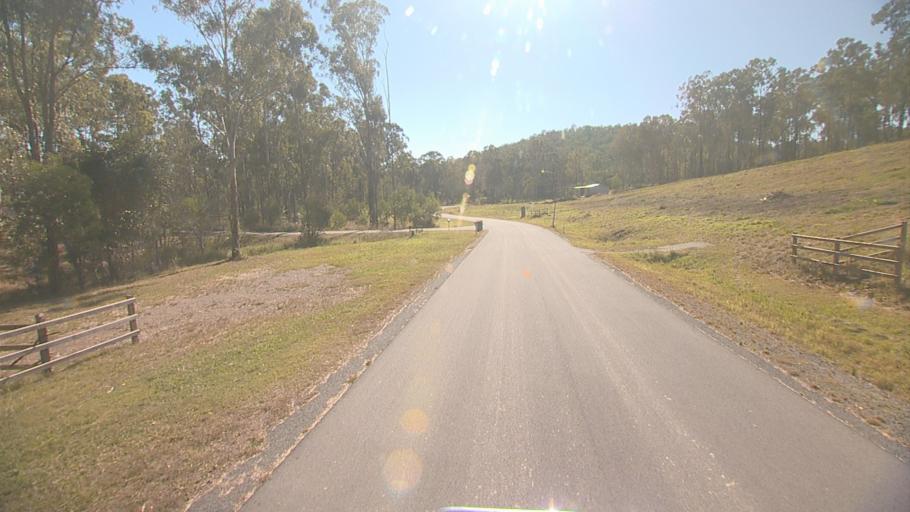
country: AU
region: Queensland
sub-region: Logan
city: Windaroo
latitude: -27.7739
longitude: 153.1458
